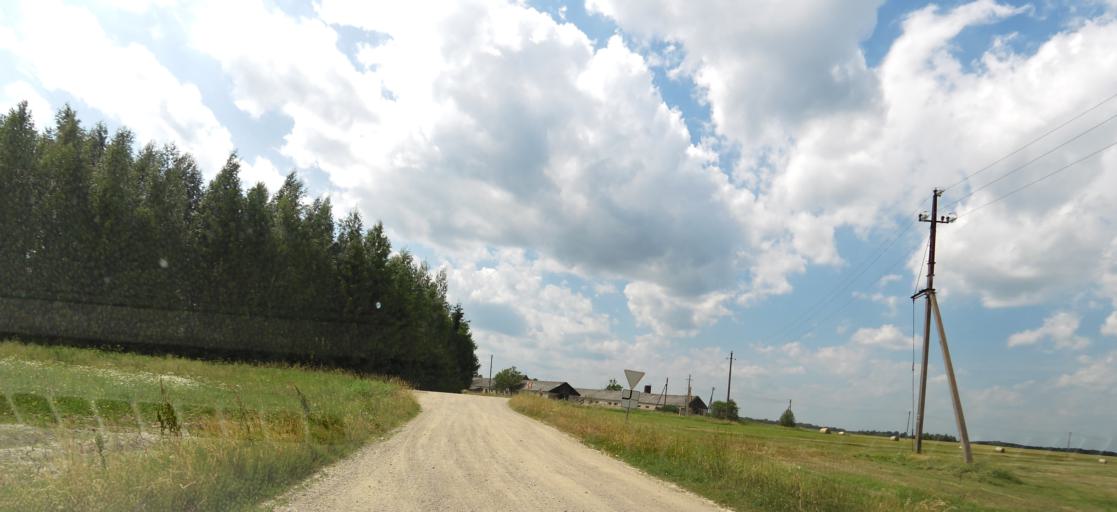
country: LT
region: Panevezys
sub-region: Birzai
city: Birzai
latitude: 56.1188
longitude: 24.8900
